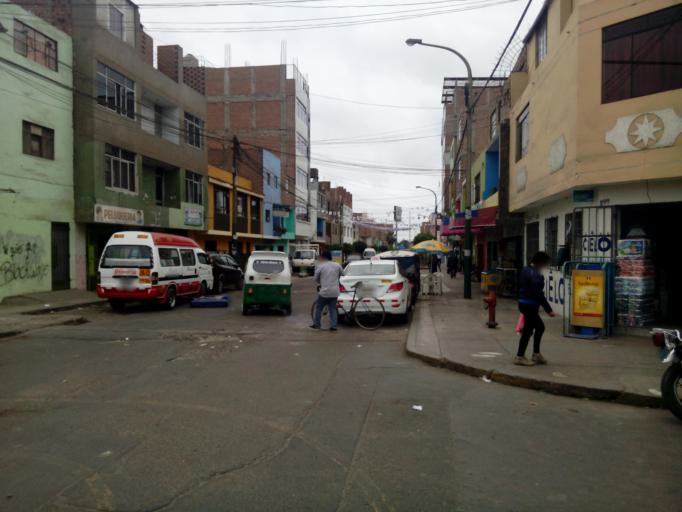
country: PE
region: Callao
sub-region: Callao
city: Callao
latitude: -12.0413
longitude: -77.0961
